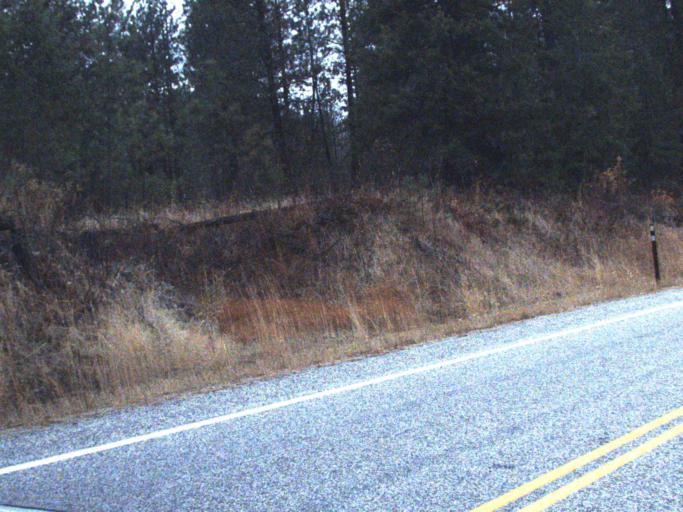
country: US
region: Washington
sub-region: Stevens County
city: Kettle Falls
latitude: 48.7719
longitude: -118.1428
